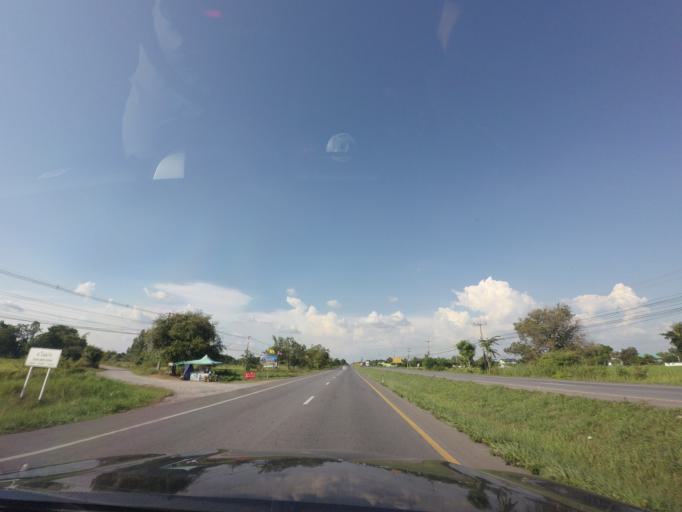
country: TH
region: Khon Kaen
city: Non Sila
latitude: 15.9868
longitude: 102.6976
